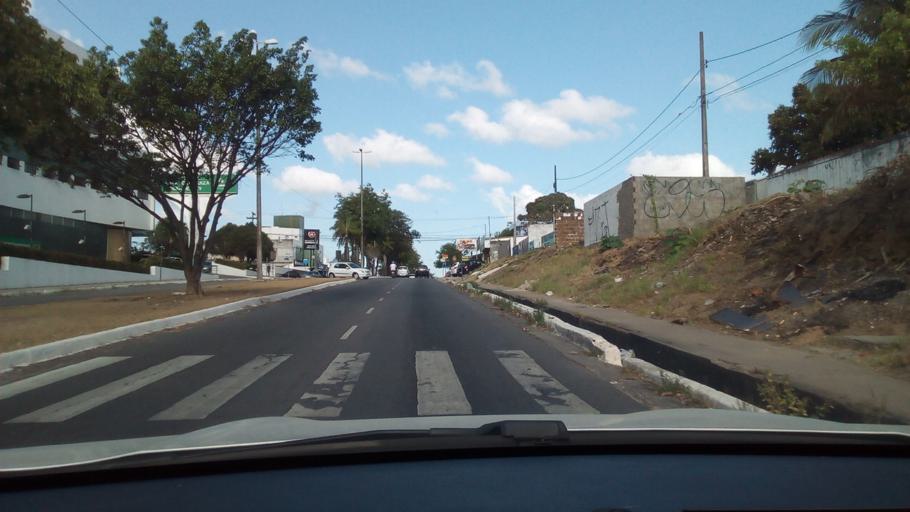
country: BR
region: Paraiba
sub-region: Joao Pessoa
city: Joao Pessoa
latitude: -7.1296
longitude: -34.8569
